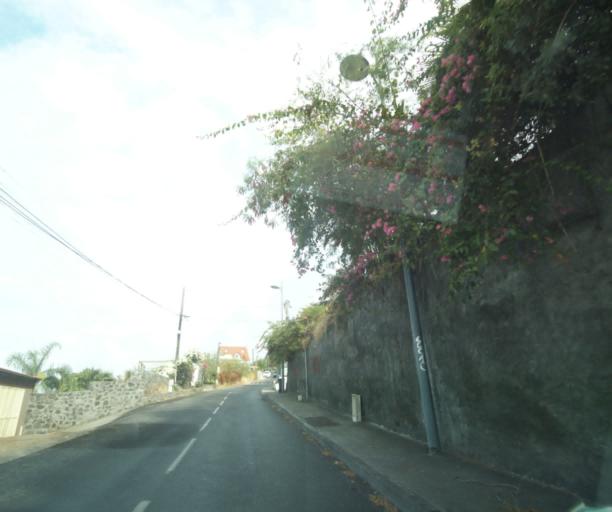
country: RE
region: Reunion
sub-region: Reunion
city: Saint-Paul
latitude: -21.0496
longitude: 55.2273
